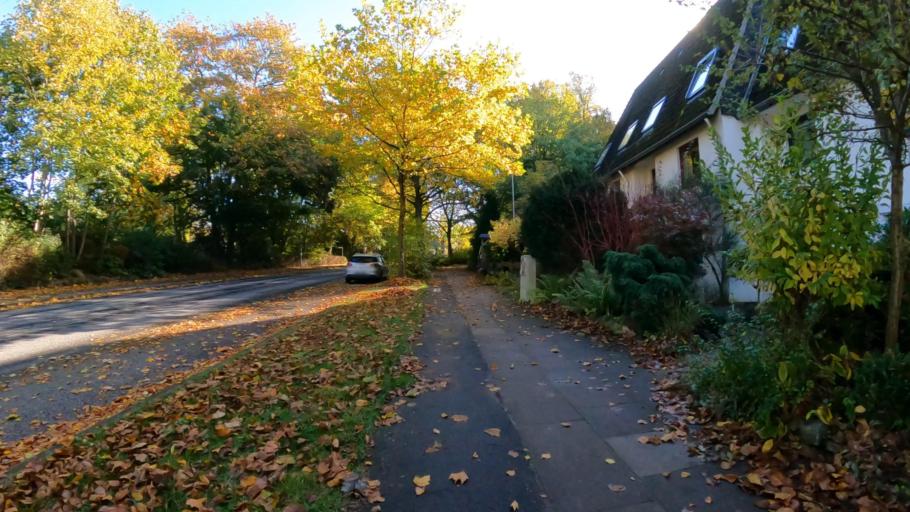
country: DE
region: Schleswig-Holstein
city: Ahrensburg
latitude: 53.6833
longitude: 10.2325
